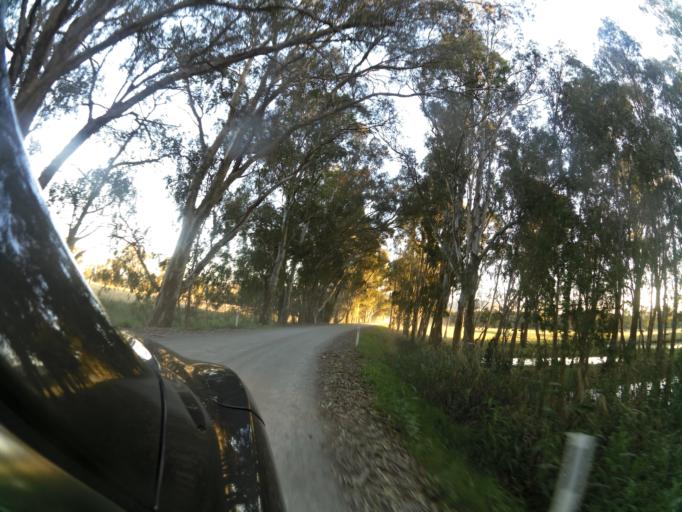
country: AU
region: Victoria
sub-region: Murrindindi
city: Alexandra
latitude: -37.1534
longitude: 145.5441
